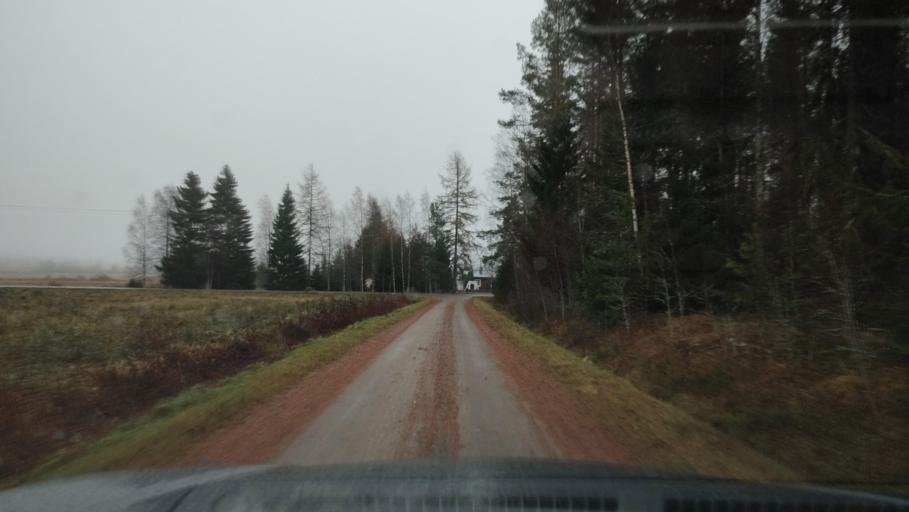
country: FI
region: Southern Ostrobothnia
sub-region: Suupohja
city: Karijoki
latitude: 62.1841
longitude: 21.7805
